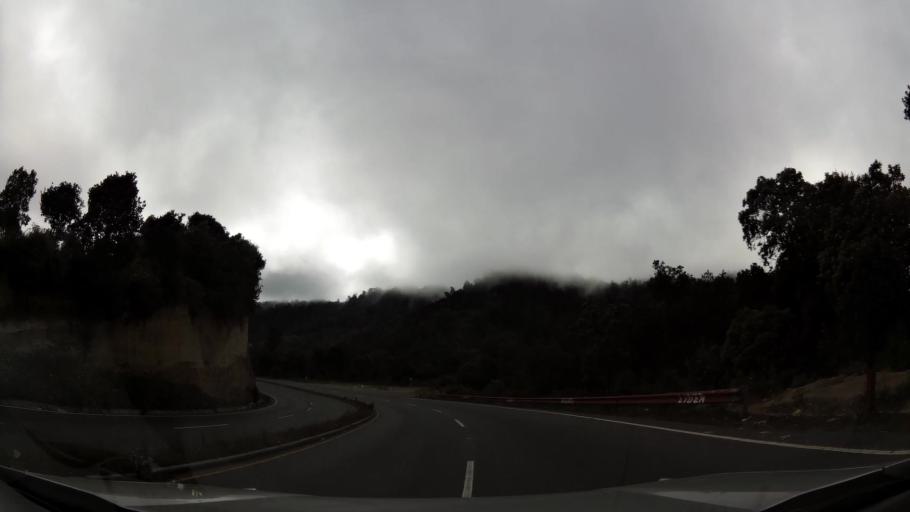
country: GT
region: Quetzaltenango
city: Cantel
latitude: 14.8426
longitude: -91.4048
